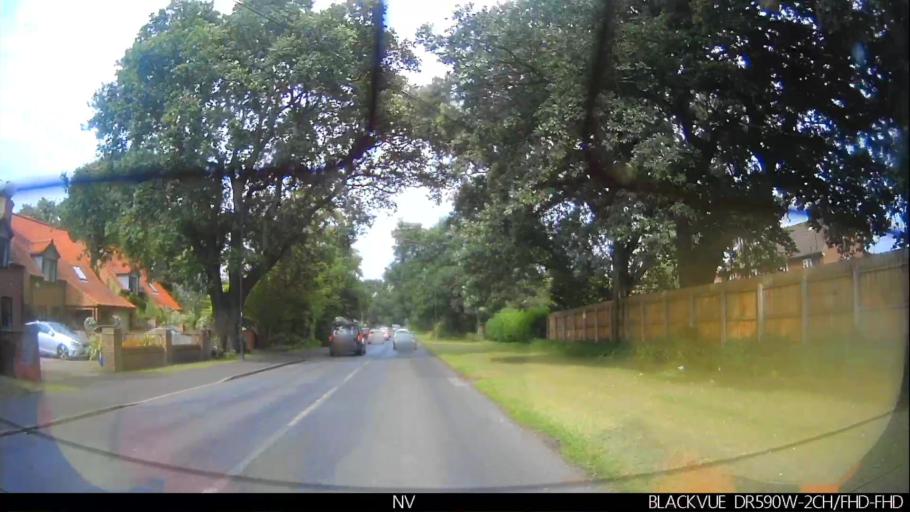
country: GB
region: England
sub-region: North Yorkshire
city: Strensall
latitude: 54.0284
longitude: -1.0393
